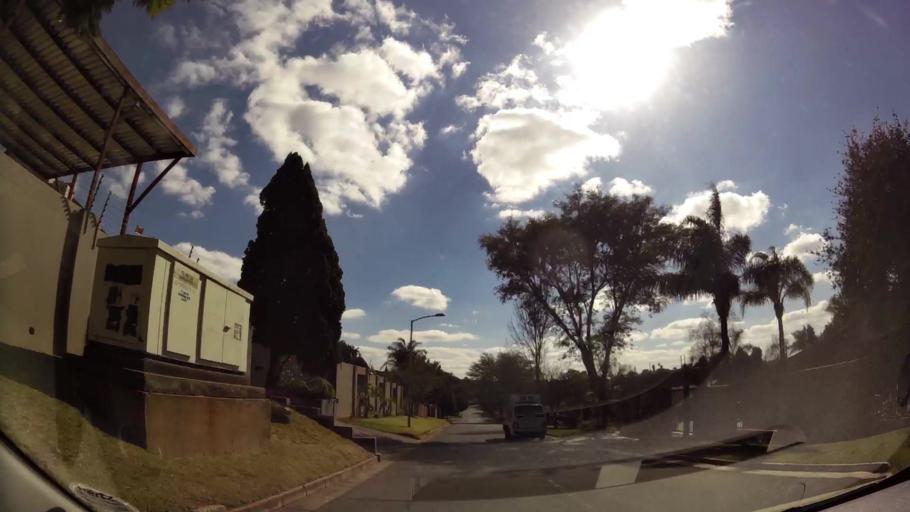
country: ZA
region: Gauteng
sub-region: West Rand District Municipality
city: Krugersdorp
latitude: -26.0882
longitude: 27.7956
